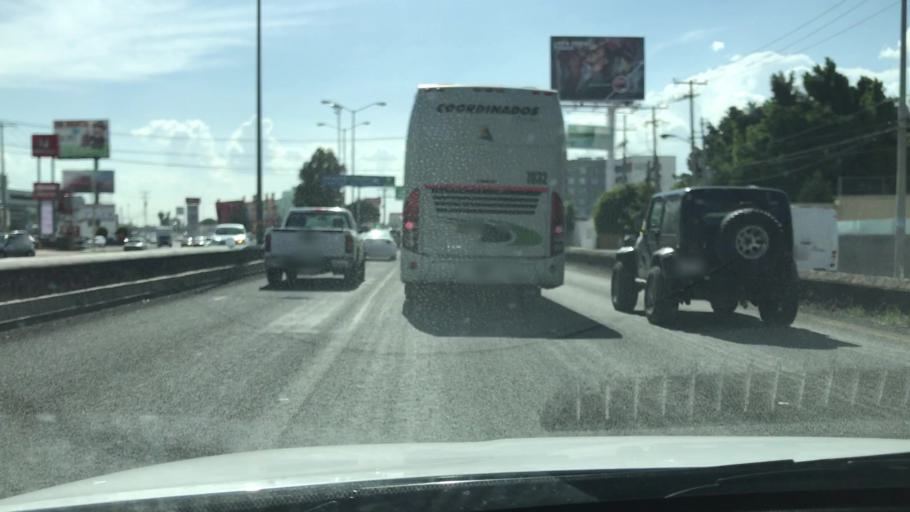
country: MX
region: Guanajuato
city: Celaya
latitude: 20.5173
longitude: -100.7878
